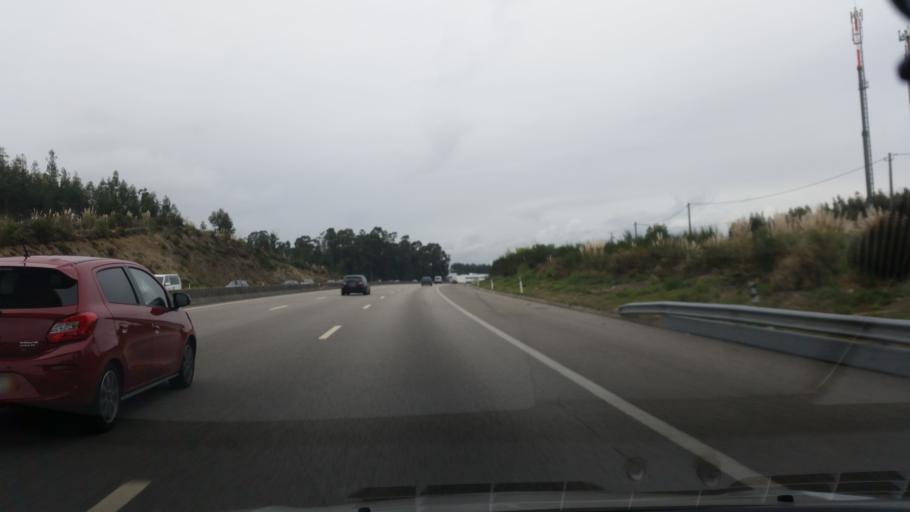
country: PT
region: Porto
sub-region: Maia
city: Nogueira
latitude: 41.2527
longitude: -8.5683
